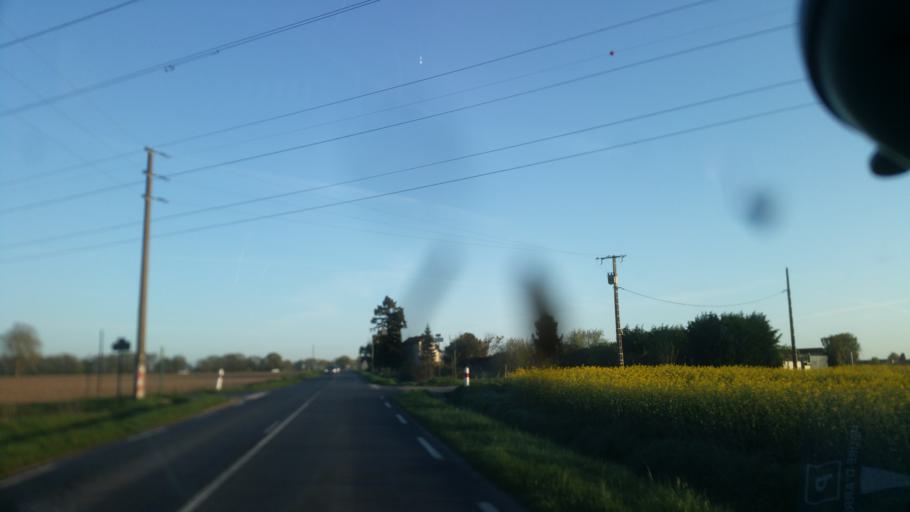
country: FR
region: Ile-de-France
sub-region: Departement de l'Essonne
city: Limours
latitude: 48.6345
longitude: 2.0639
